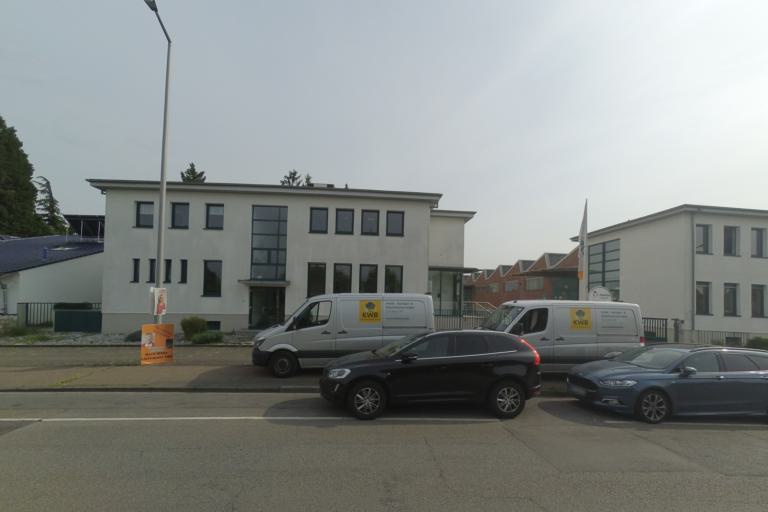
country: DE
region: Baden-Wuerttemberg
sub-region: Karlsruhe Region
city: Mannheim
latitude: 49.5146
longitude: 8.5029
